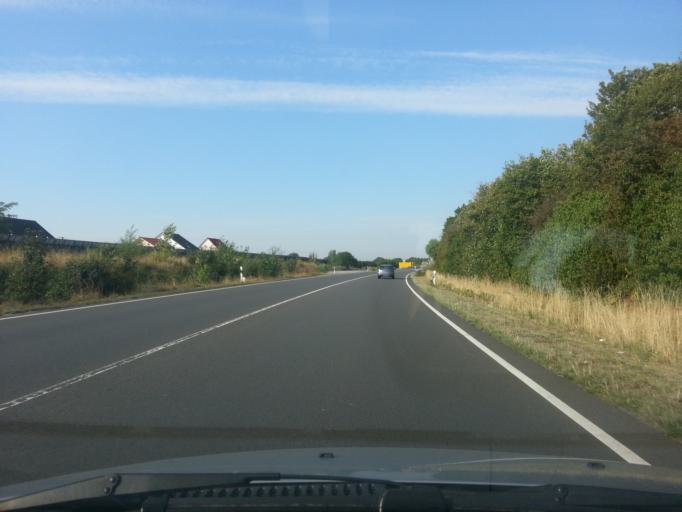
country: DE
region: Hesse
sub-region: Regierungsbezirk Darmstadt
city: Burstadt
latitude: 49.6383
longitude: 8.4734
